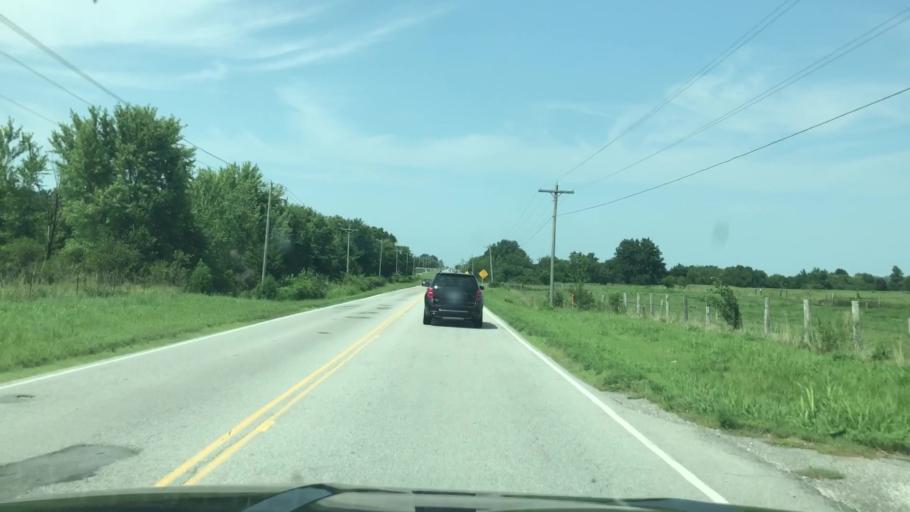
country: US
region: Oklahoma
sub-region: Ottawa County
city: Miami
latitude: 36.8938
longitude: -94.8418
